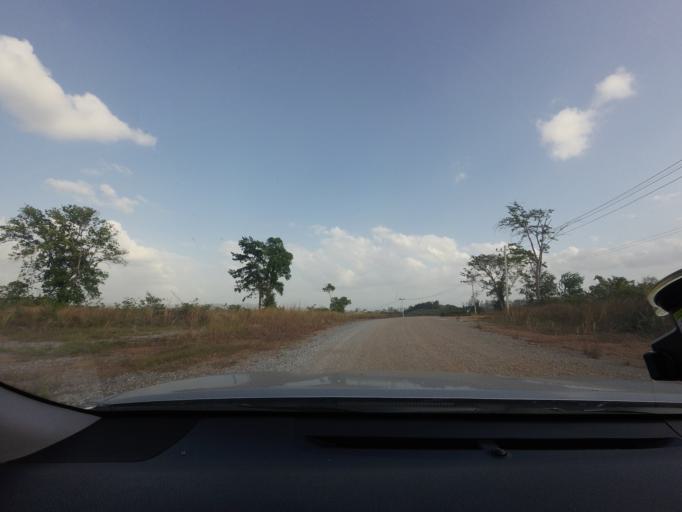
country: TH
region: Pattani
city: Mae Lan
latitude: 6.6054
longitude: 101.2474
